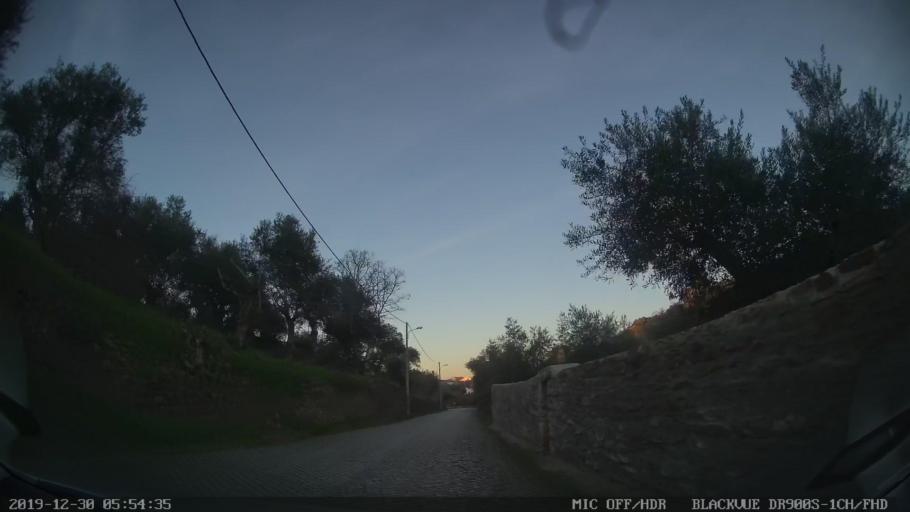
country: PT
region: Castelo Branco
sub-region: Idanha-A-Nova
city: Idanha-a-Nova
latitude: 40.0212
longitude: -7.2451
